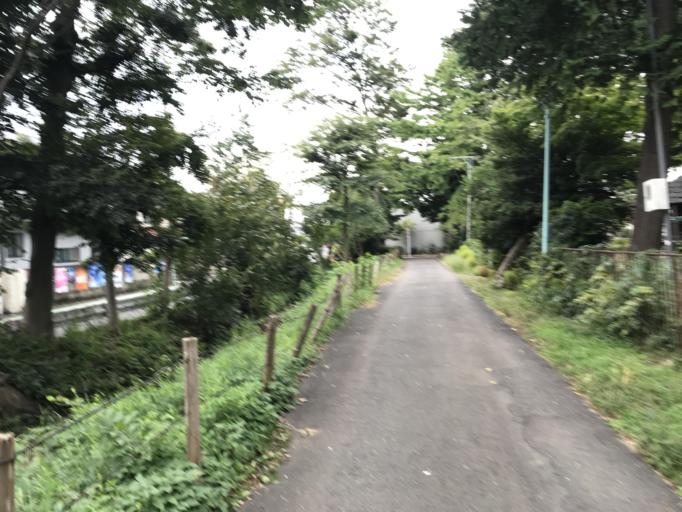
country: JP
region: Tokyo
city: Higashimurayama-shi
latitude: 35.7515
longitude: 139.4818
